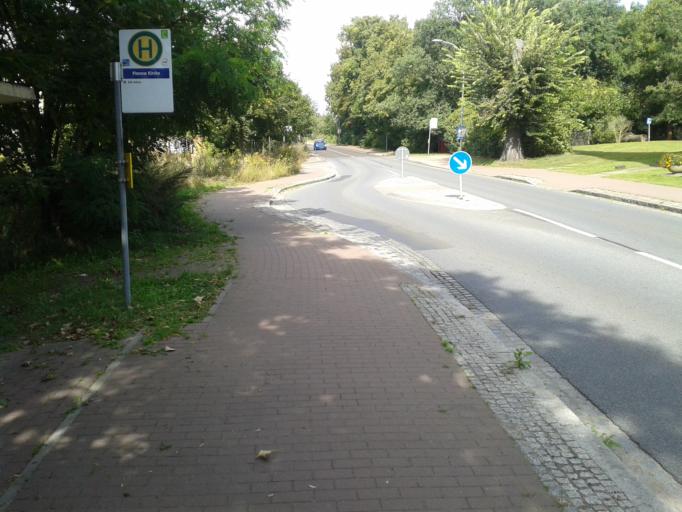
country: DE
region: Brandenburg
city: Hohen Neuendorf
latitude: 52.7039
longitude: 13.2473
